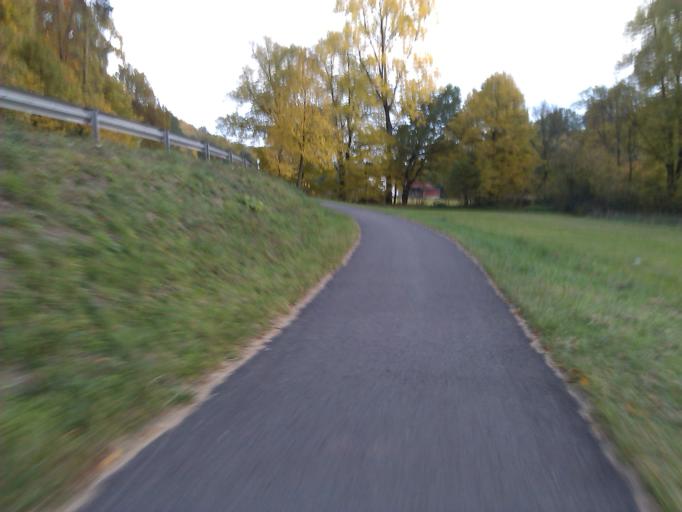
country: DE
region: Rheinland-Pfalz
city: Otterberg
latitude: 49.5121
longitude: 7.7567
